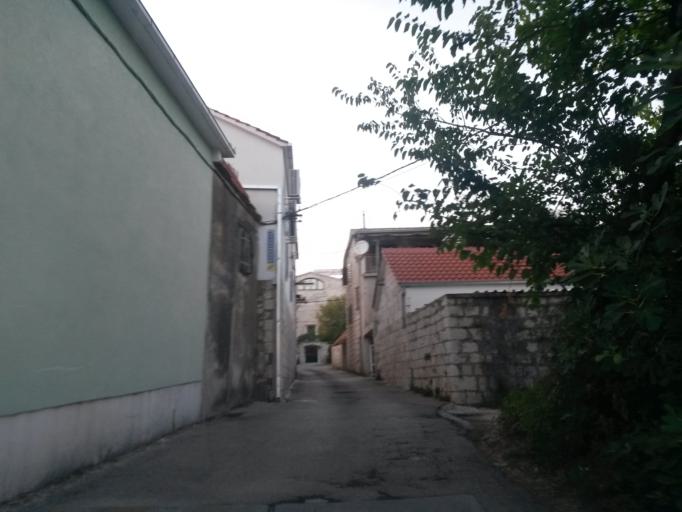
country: HR
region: Splitsko-Dalmatinska
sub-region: Grad Trogir
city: Trogir
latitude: 43.5122
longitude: 16.1836
